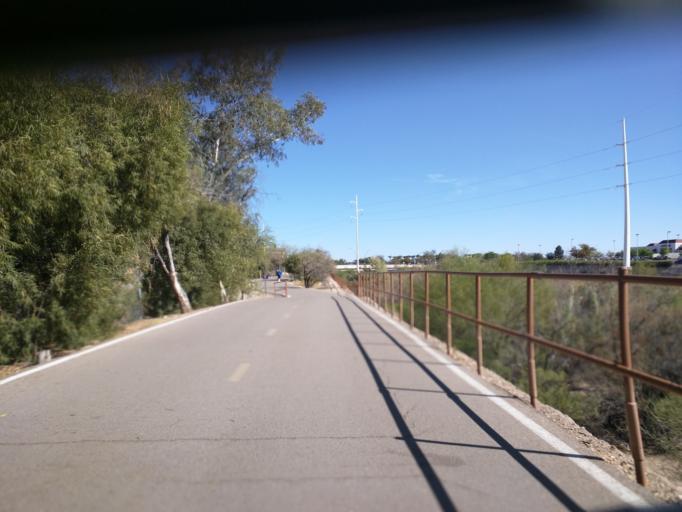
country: US
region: Arizona
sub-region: Pima County
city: Flowing Wells
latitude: 32.2917
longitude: -110.9727
